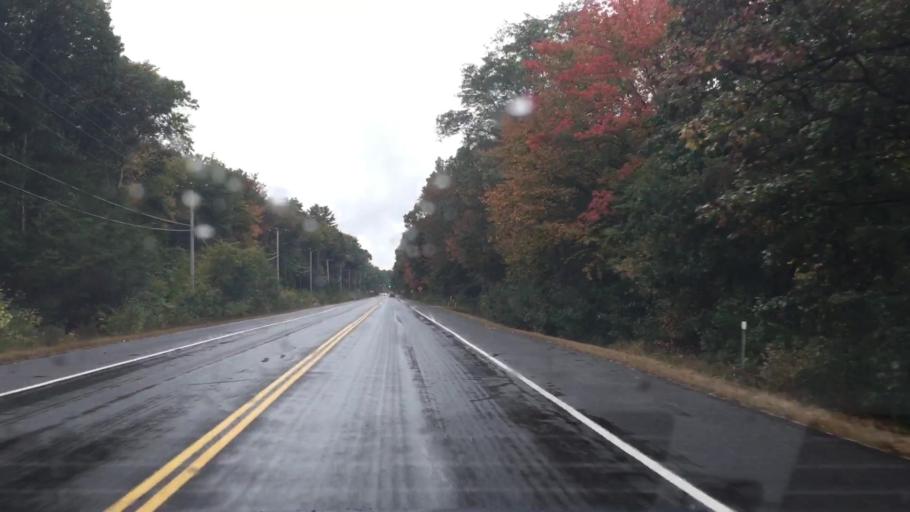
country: US
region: Massachusetts
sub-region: Essex County
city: Salisbury
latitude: 42.8704
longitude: -70.8479
